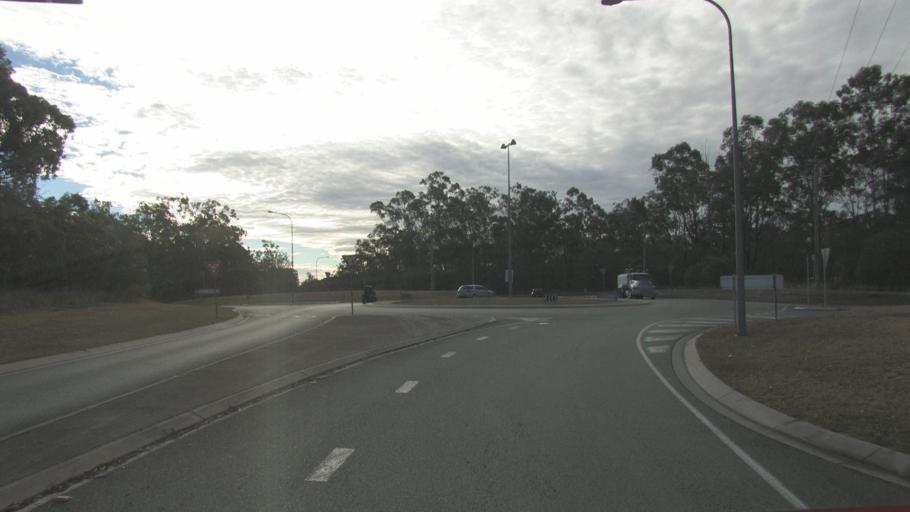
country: AU
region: Queensland
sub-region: Logan
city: Cedar Vale
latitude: -27.8361
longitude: 153.0460
